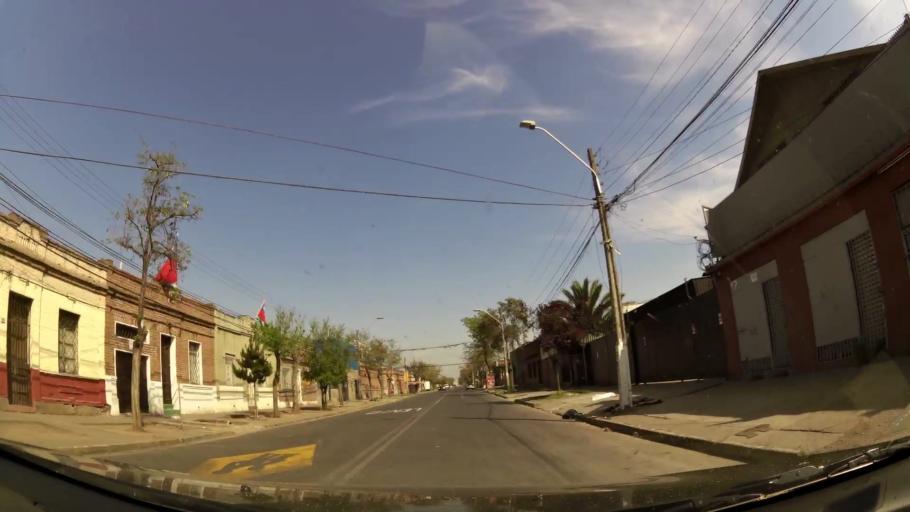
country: CL
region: Santiago Metropolitan
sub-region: Provincia de Santiago
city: Santiago
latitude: -33.4063
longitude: -70.6343
